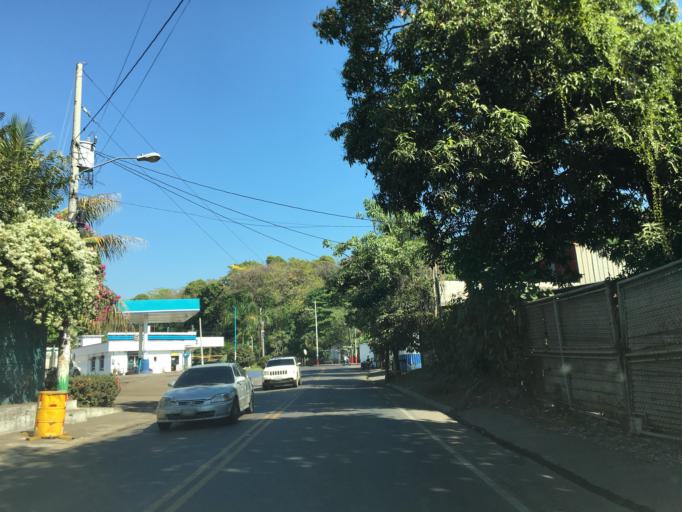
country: GT
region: Escuintla
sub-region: Municipio de La Democracia
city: La Democracia
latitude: 14.2334
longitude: -90.9502
